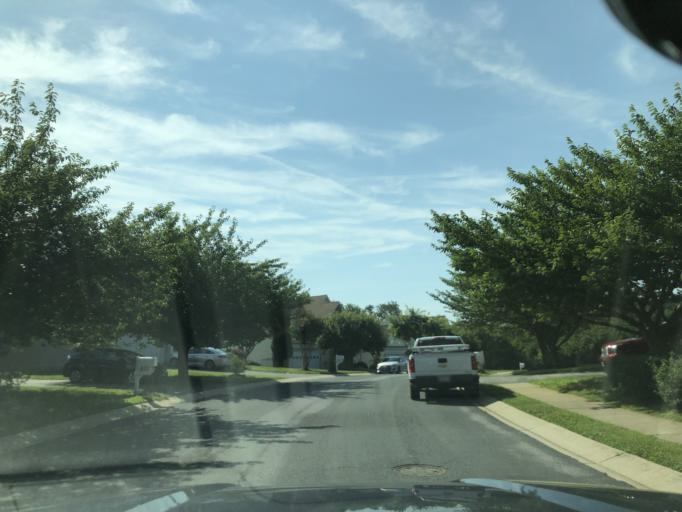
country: US
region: Maryland
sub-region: Carroll County
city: Eldersburg
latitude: 39.4114
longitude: -76.9658
